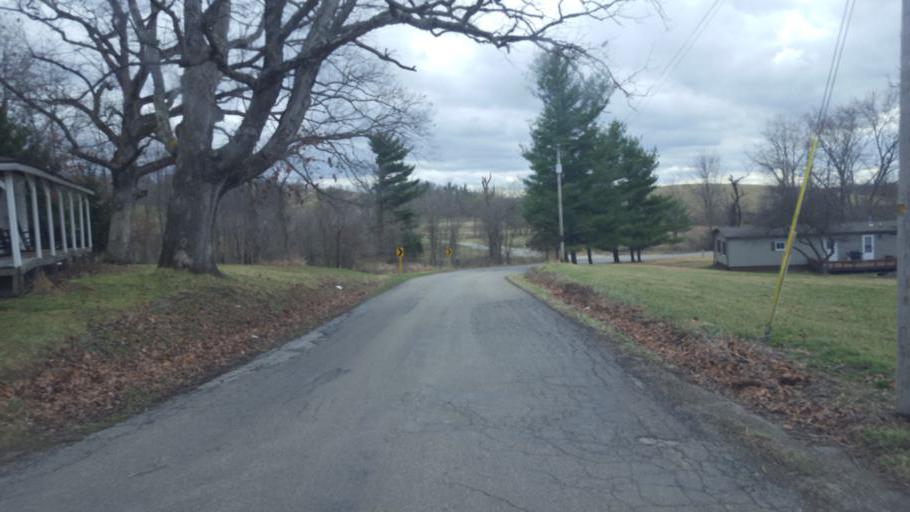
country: US
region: Ohio
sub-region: Muskingum County
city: Frazeysburg
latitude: 40.0987
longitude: -82.2009
